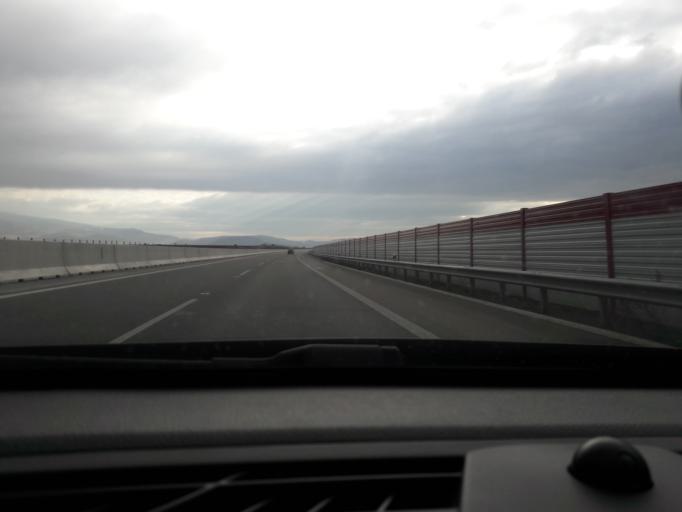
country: SK
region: Banskobystricky
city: Hrochot,Slovakia
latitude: 48.5725
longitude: 19.2591
